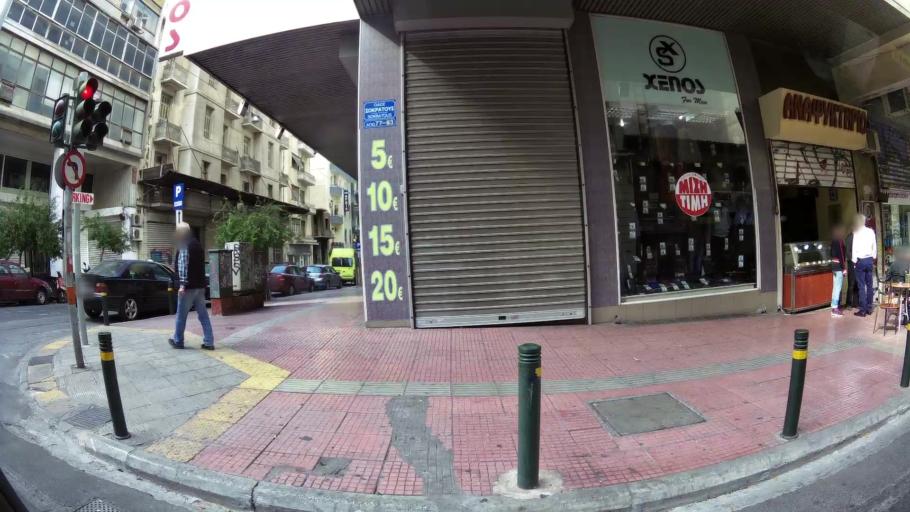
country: GR
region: Attica
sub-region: Nomarchia Athinas
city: Athens
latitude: 37.9858
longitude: 23.7272
